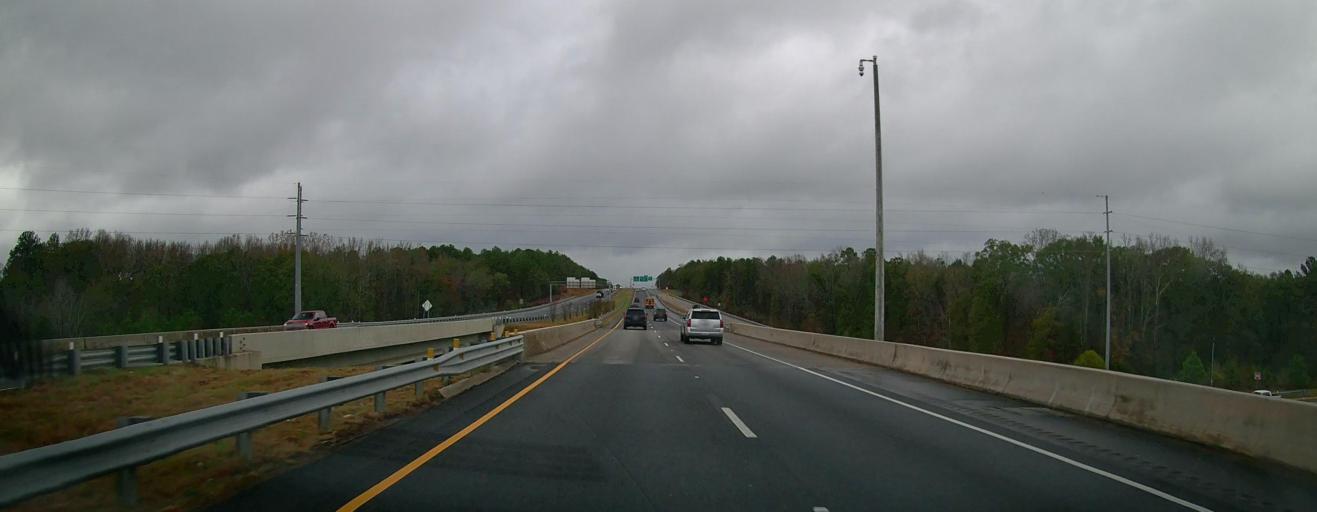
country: US
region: Georgia
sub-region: Clarke County
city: Athens
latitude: 33.9632
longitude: -83.3526
